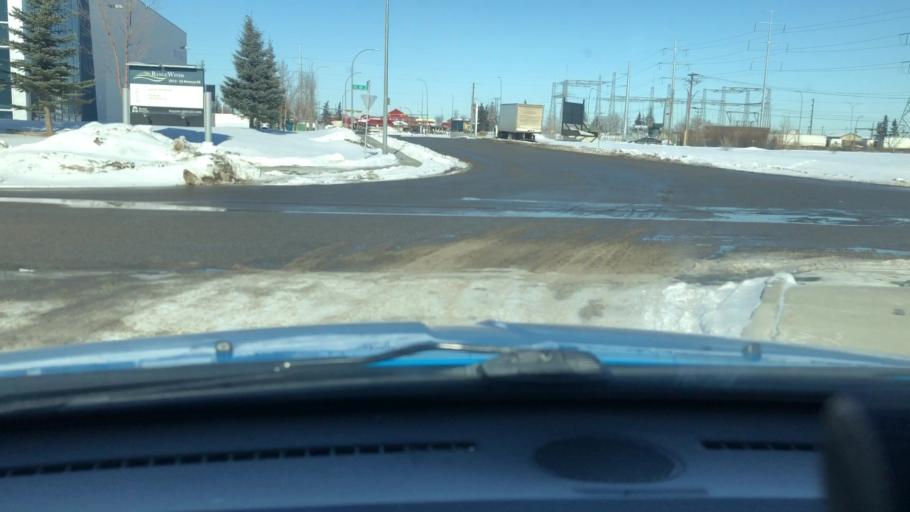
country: CA
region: Alberta
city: Calgary
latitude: 51.0067
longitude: -114.0043
